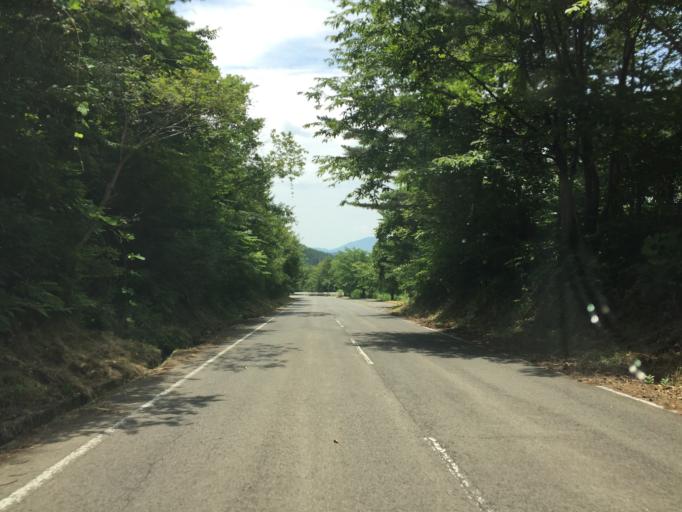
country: JP
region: Fukushima
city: Hobaramachi
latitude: 37.6741
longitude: 140.6570
